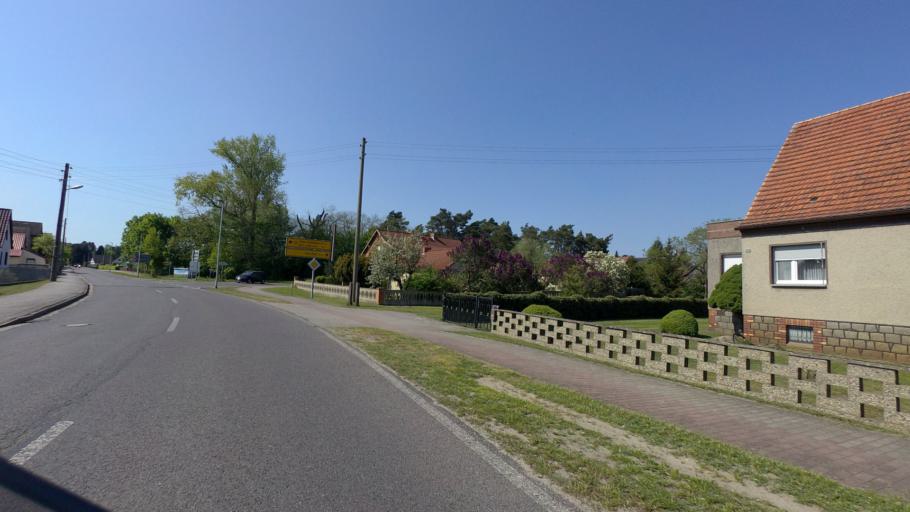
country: DE
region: Brandenburg
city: Schlepzig
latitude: 52.0530
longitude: 13.9925
